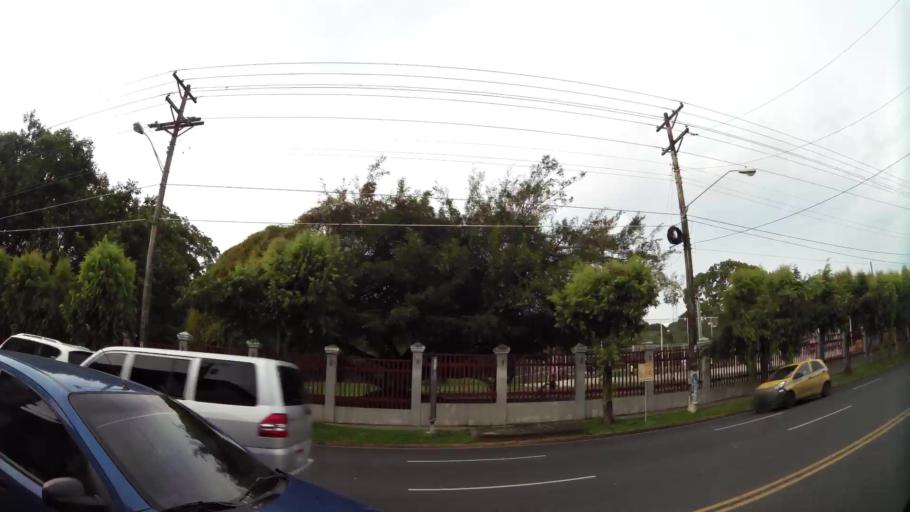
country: PA
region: Panama
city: Panama
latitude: 8.9969
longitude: -79.5091
